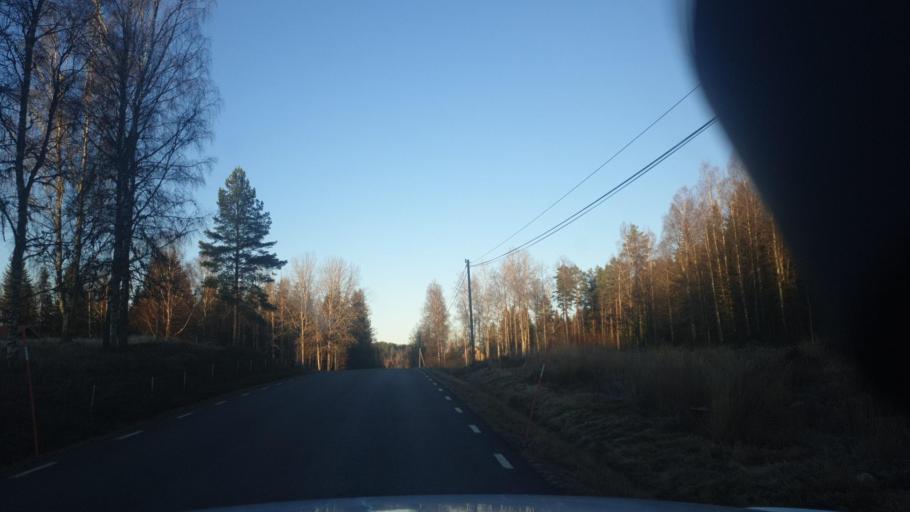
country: SE
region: Vaermland
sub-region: Eda Kommun
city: Amotfors
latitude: 59.9228
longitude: 12.5209
